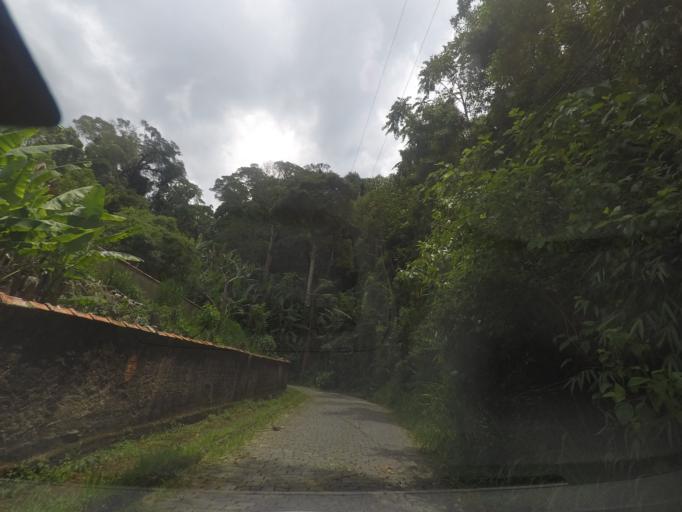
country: BR
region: Rio de Janeiro
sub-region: Petropolis
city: Petropolis
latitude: -22.5000
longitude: -43.1871
